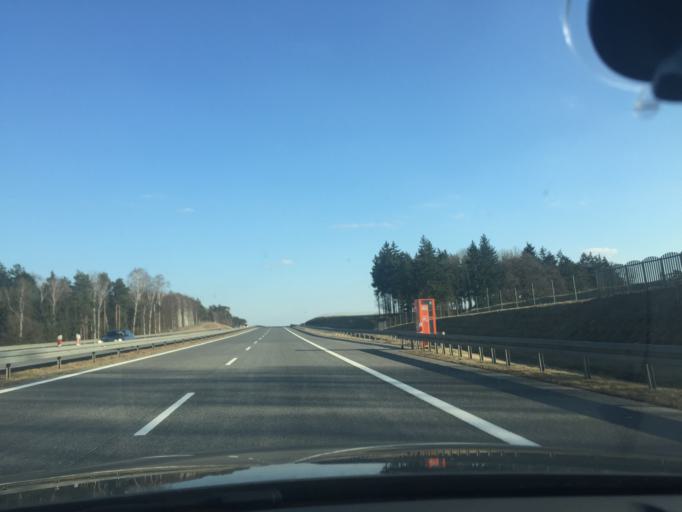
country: PL
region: Lubusz
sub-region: Powiat miedzyrzecki
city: Brojce
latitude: 52.3070
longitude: 15.6273
